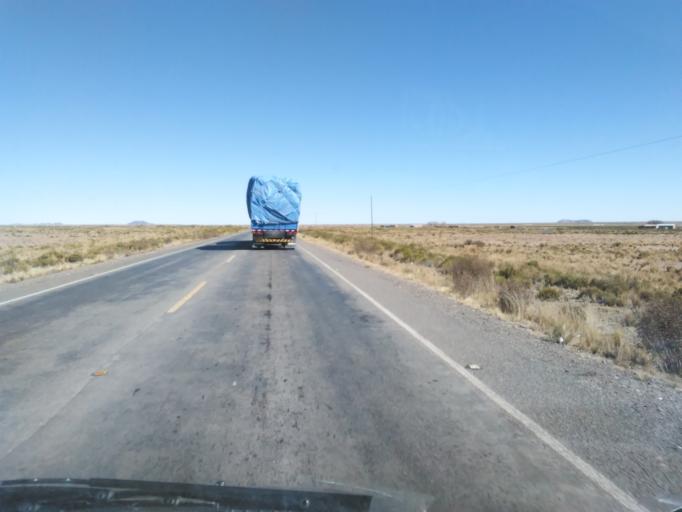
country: BO
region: Oruro
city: Machacamarca
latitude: -18.0852
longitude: -67.0091
